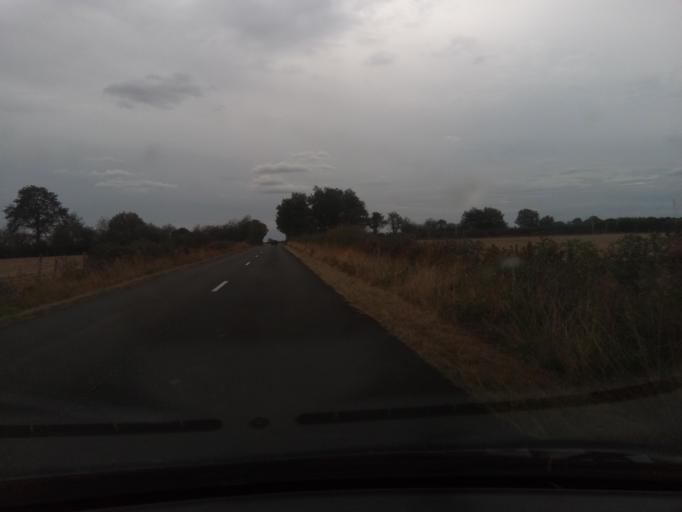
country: FR
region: Poitou-Charentes
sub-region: Departement de la Vienne
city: Pleumartin
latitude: 46.6558
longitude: 0.7818
